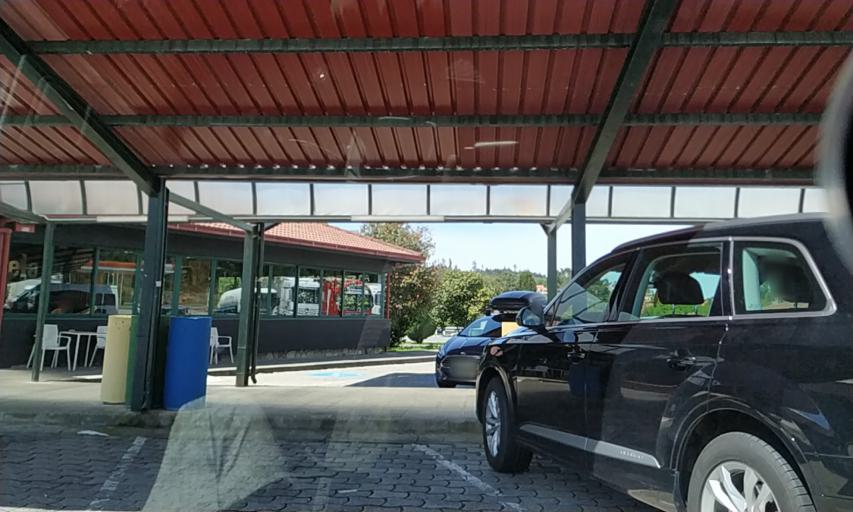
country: ES
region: Galicia
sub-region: Provincia da Coruna
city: Santiago de Compostela
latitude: 42.8108
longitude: -8.5866
